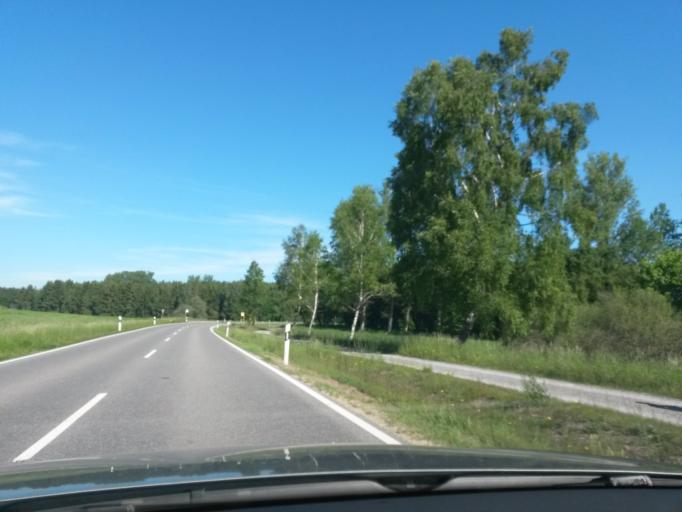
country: DE
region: Baden-Wuerttemberg
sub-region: Tuebingen Region
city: Bad Buchau
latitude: 48.0446
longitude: 9.6281
